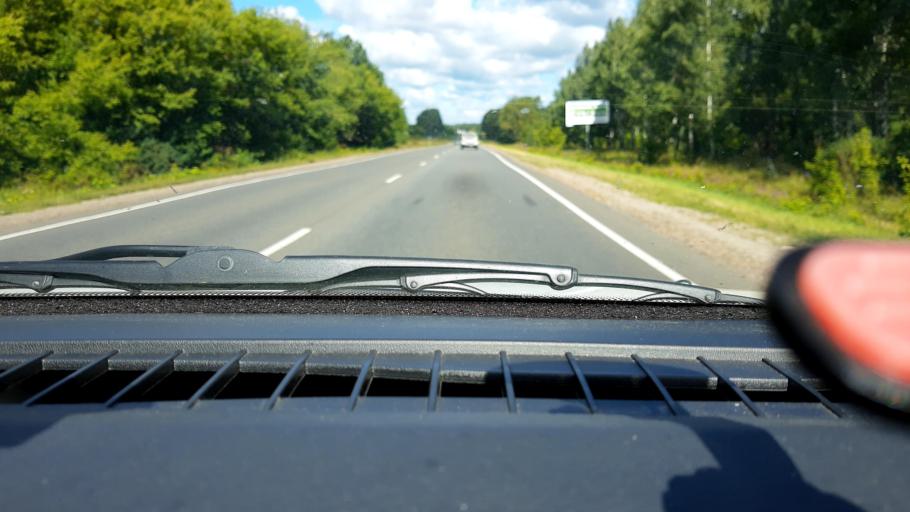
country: RU
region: Nizjnij Novgorod
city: Arzamas
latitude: 55.2876
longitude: 43.9471
